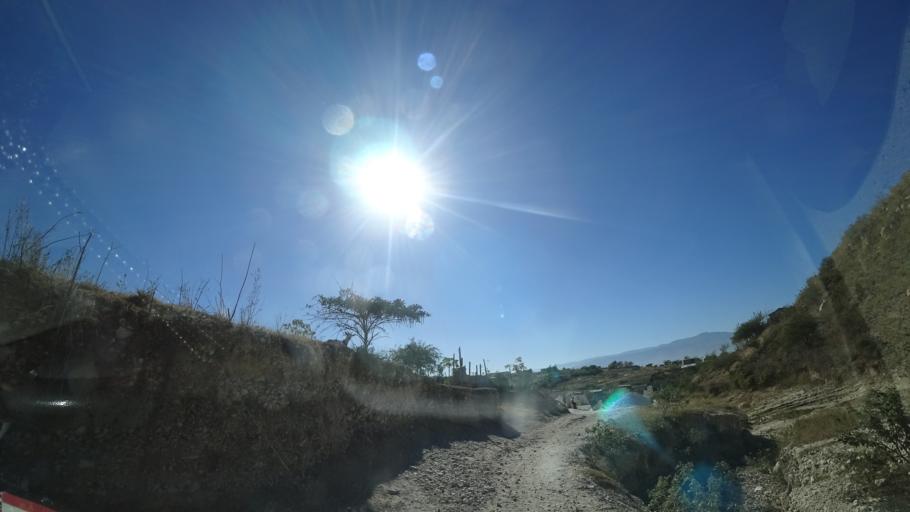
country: HT
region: Ouest
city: Croix des Bouquets
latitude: 18.6716
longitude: -72.2853
